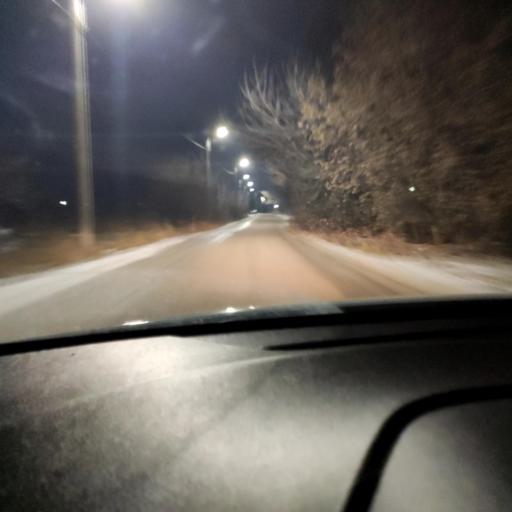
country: RU
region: Tatarstan
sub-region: Gorod Kazan'
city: Kazan
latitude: 55.7250
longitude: 49.1004
